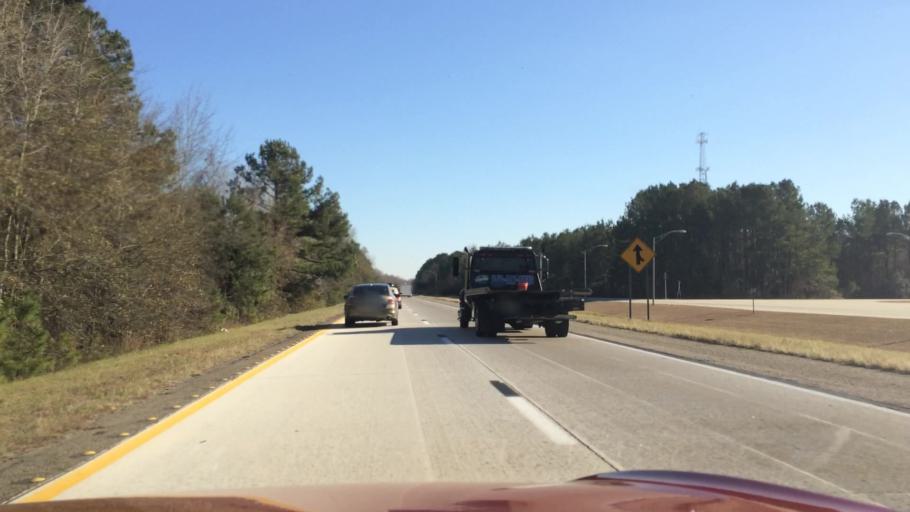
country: US
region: South Carolina
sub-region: Orangeburg County
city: Holly Hill
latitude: 33.2694
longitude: -80.4872
